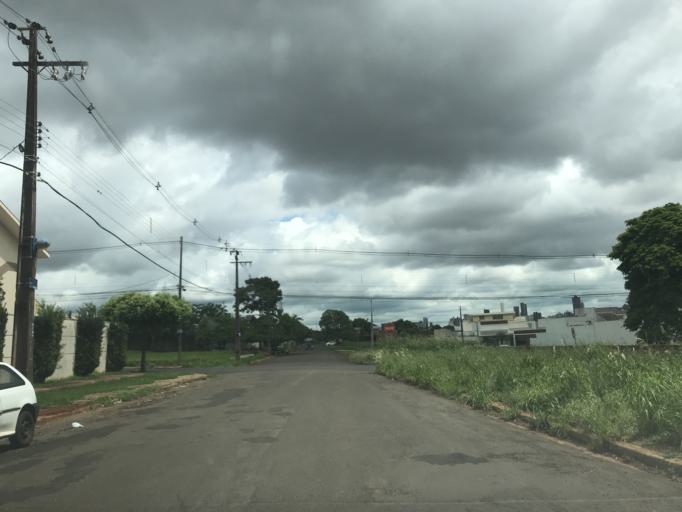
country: BR
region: Parana
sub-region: Maringa
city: Maringa
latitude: -23.4484
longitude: -51.9489
